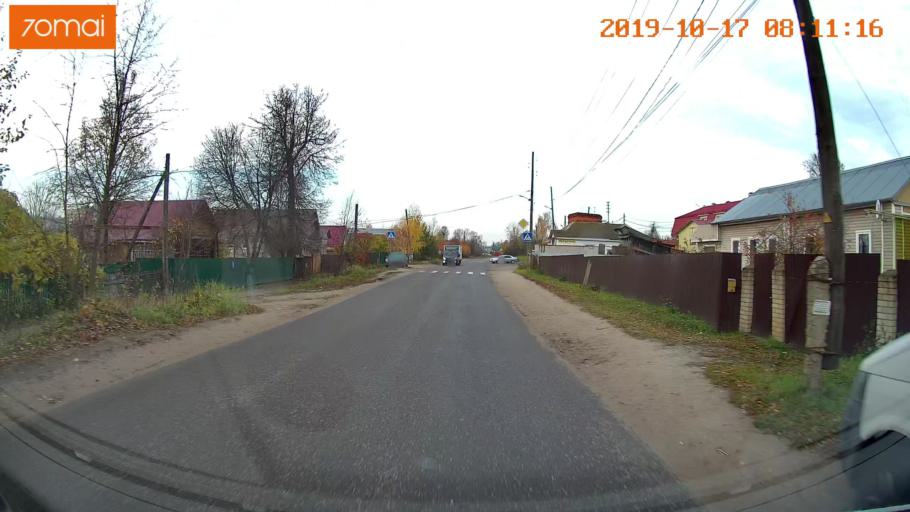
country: RU
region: Vladimir
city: Kol'chugino
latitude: 56.3037
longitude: 39.3723
